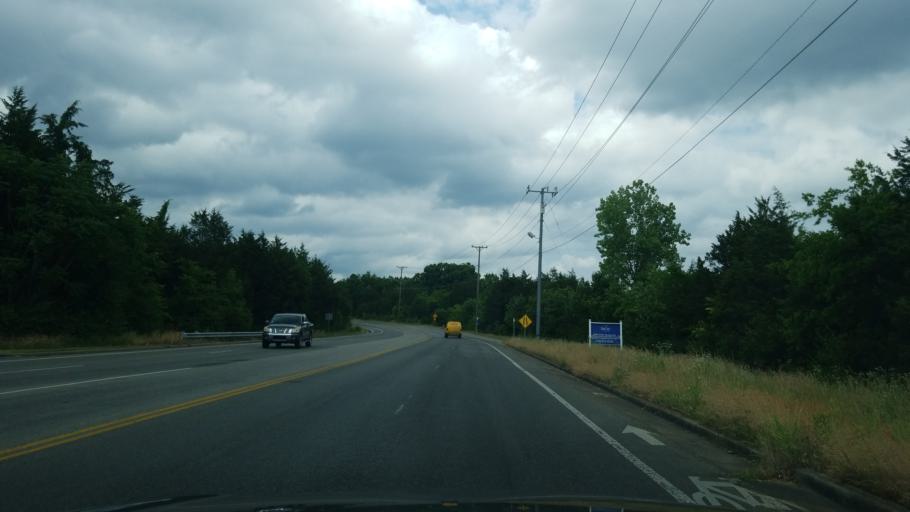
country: US
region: Tennessee
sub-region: Rutherford County
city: La Vergne
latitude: 36.0905
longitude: -86.6262
